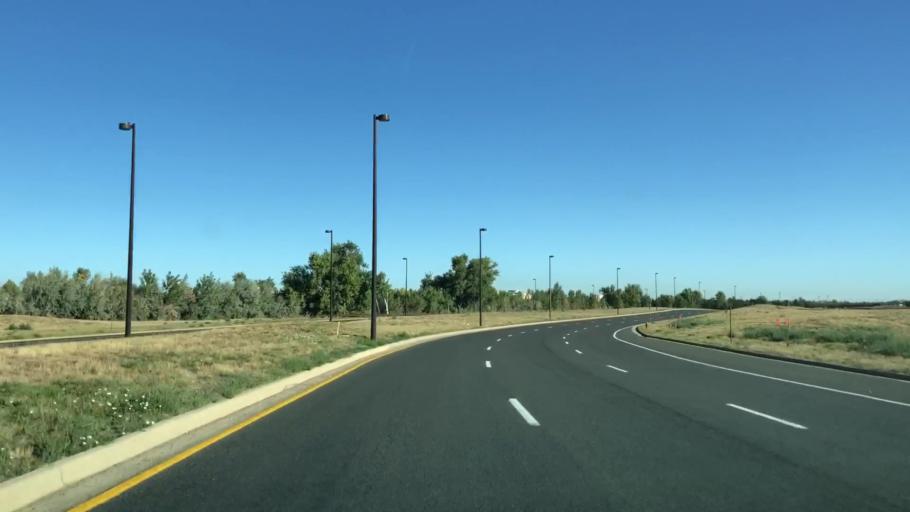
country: US
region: Colorado
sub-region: Larimer County
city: Loveland
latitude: 40.4120
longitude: -104.9864
